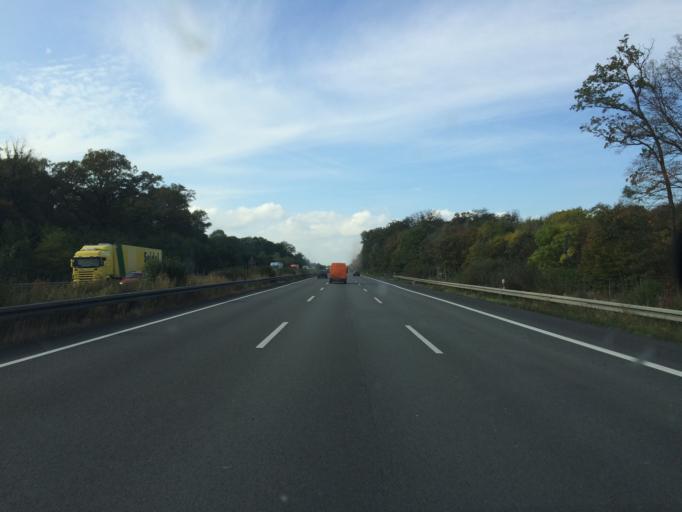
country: DE
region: Lower Saxony
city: Lehre
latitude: 52.3090
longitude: 10.6808
